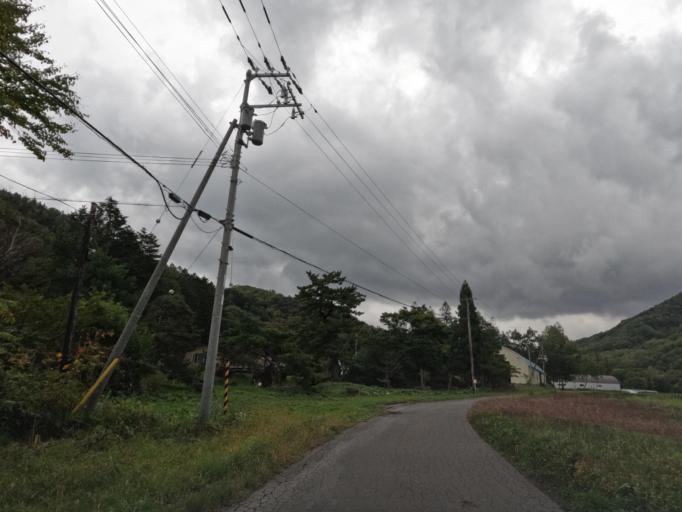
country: JP
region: Hokkaido
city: Date
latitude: 42.5010
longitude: 140.9048
